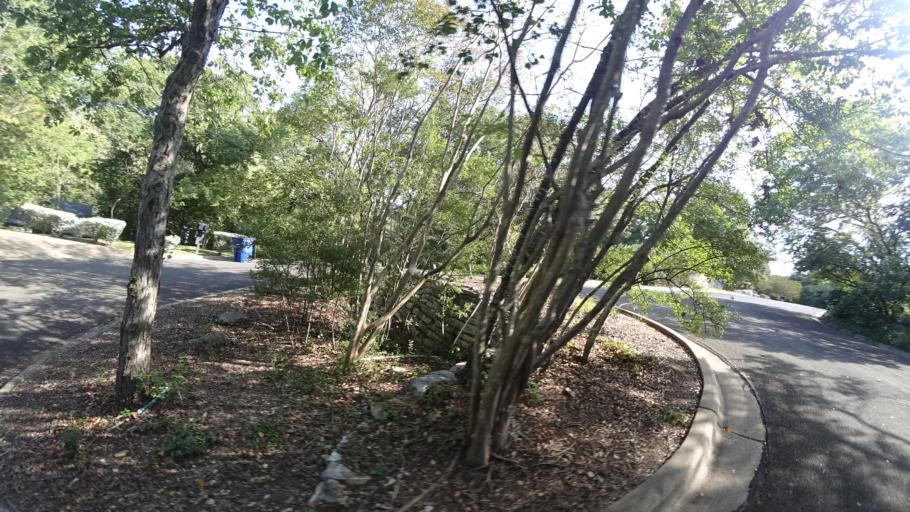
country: US
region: Texas
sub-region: Travis County
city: West Lake Hills
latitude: 30.3452
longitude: -97.7558
